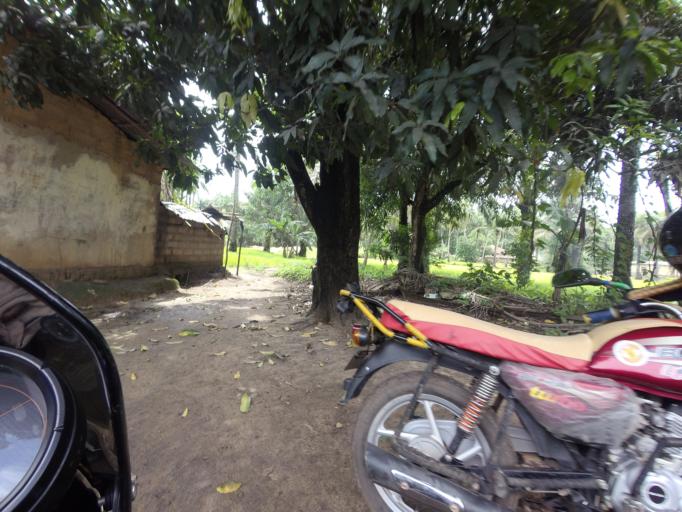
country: SL
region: Northern Province
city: Mambolo
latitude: 8.9745
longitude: -12.9961
